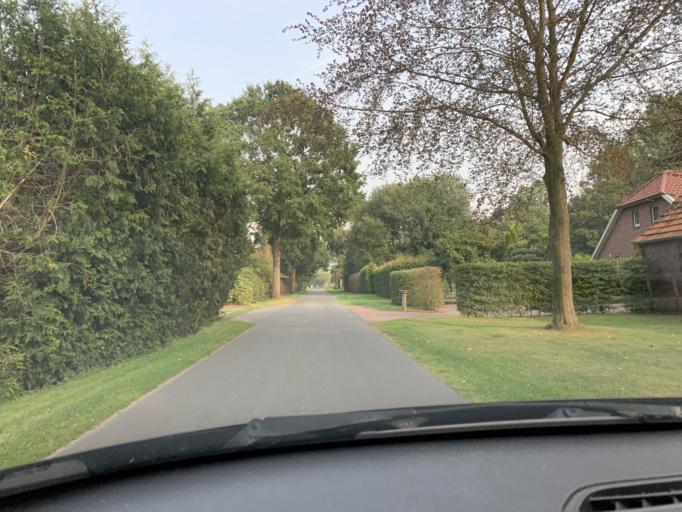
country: DE
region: Lower Saxony
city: Westerstede
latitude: 53.2579
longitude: 7.8885
